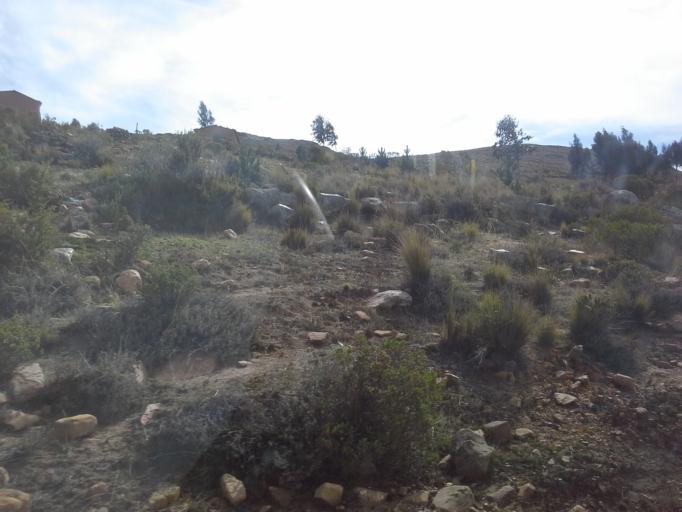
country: BO
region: Cochabamba
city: Colomi
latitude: -17.4384
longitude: -65.8357
